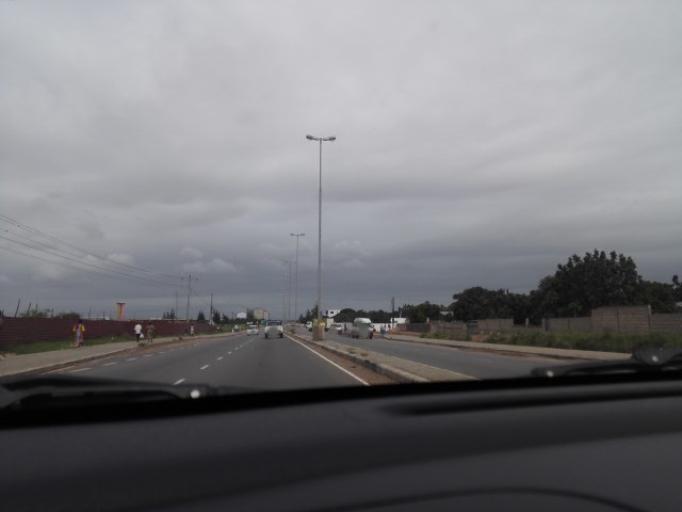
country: MZ
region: Maputo City
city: Maputo
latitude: -25.8219
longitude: 32.5868
